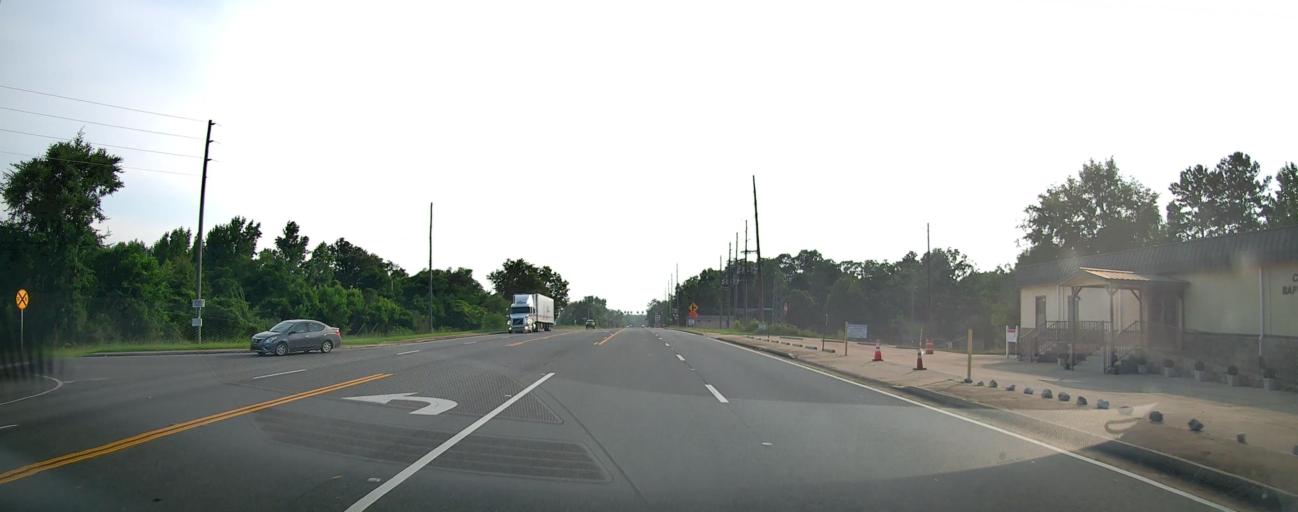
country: US
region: Georgia
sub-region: Talbot County
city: Talbotton
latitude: 32.5801
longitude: -84.5498
